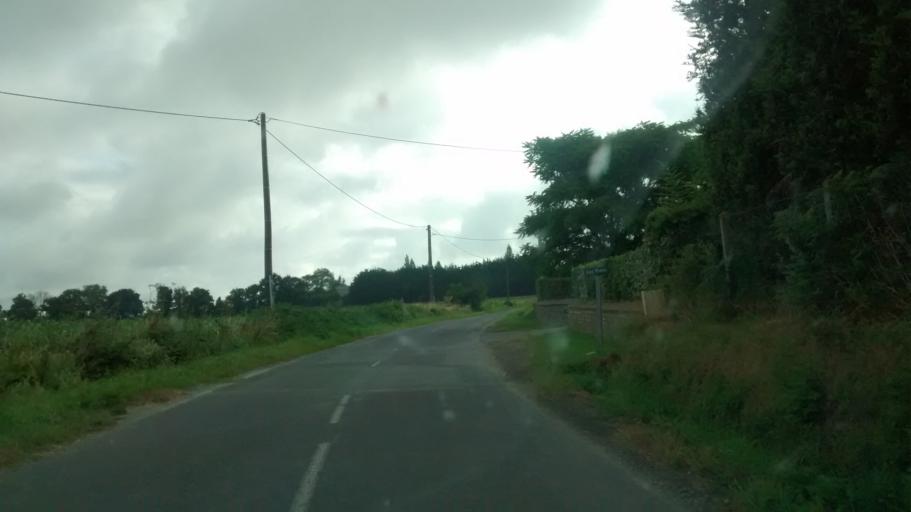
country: FR
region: Brittany
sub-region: Departement d'Ille-et-Vilaine
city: La Gouesniere
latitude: 48.5910
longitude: -1.9038
